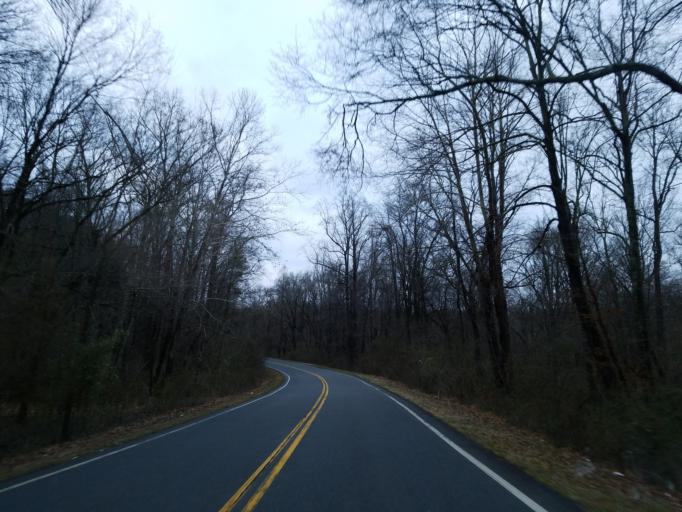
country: US
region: Georgia
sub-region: Bartow County
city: Emerson
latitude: 34.1102
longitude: -84.7482
